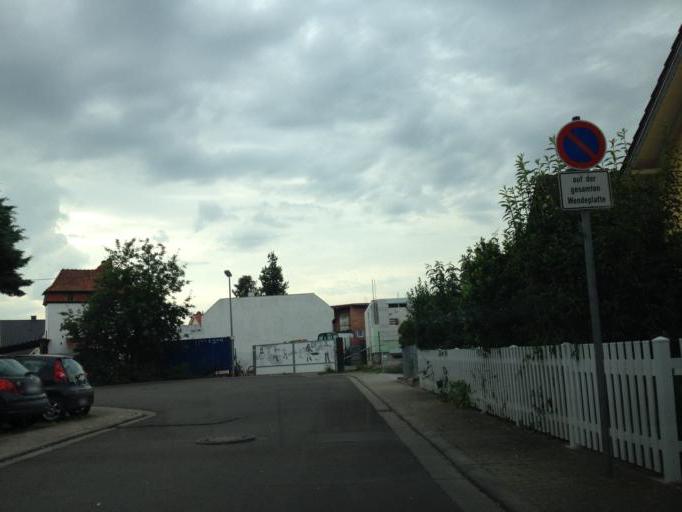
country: DE
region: Rheinland-Pfalz
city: Gau-Odernheim
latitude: 49.7813
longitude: 8.1921
